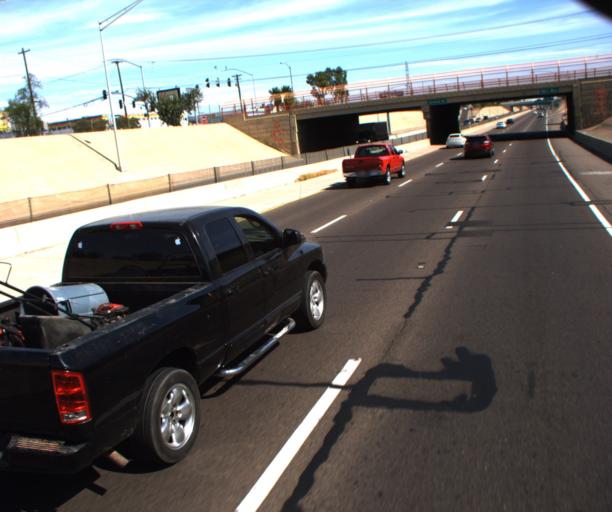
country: US
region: Arizona
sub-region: Maricopa County
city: Phoenix
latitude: 33.4360
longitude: -112.1080
